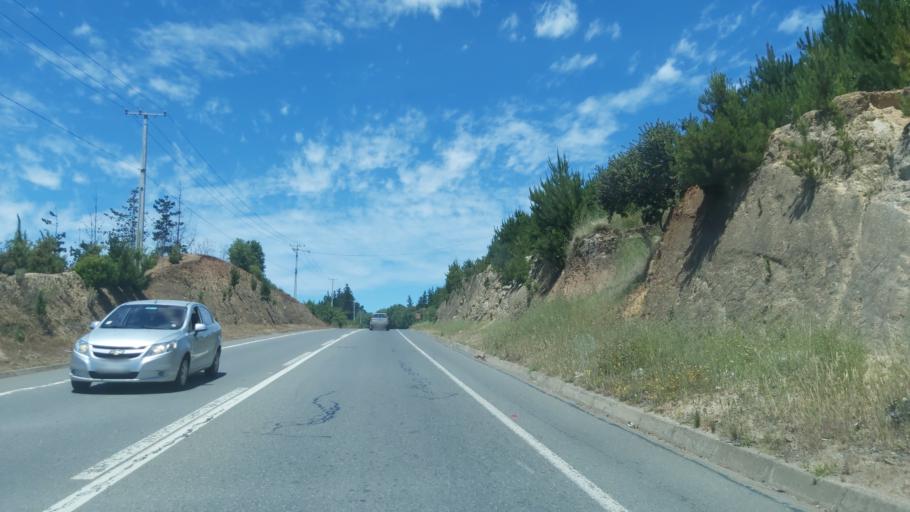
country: CL
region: Maule
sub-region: Provincia de Talca
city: Constitucion
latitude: -35.3223
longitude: -72.3854
